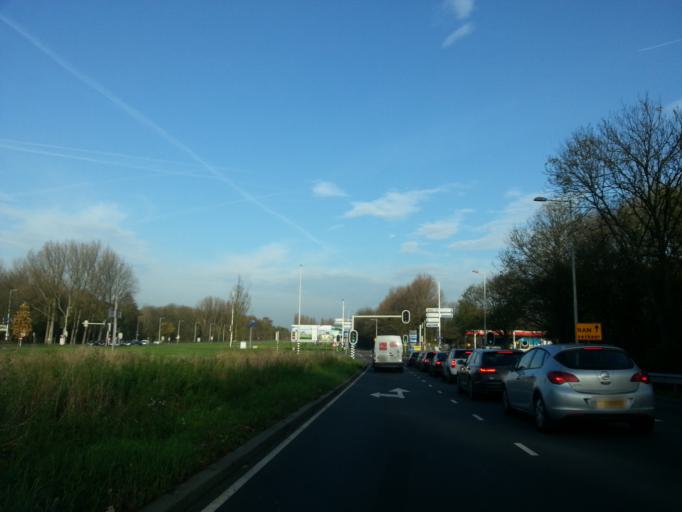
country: NL
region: South Holland
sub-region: Gemeente Rotterdam
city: Rotterdam
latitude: 51.9478
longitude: 4.4602
